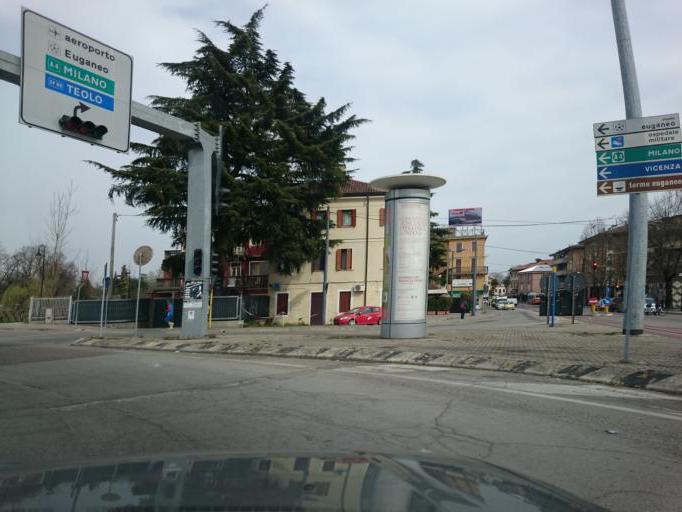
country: IT
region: Veneto
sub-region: Provincia di Padova
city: Mandriola-Sant'Agostino
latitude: 45.3868
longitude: 11.8668
